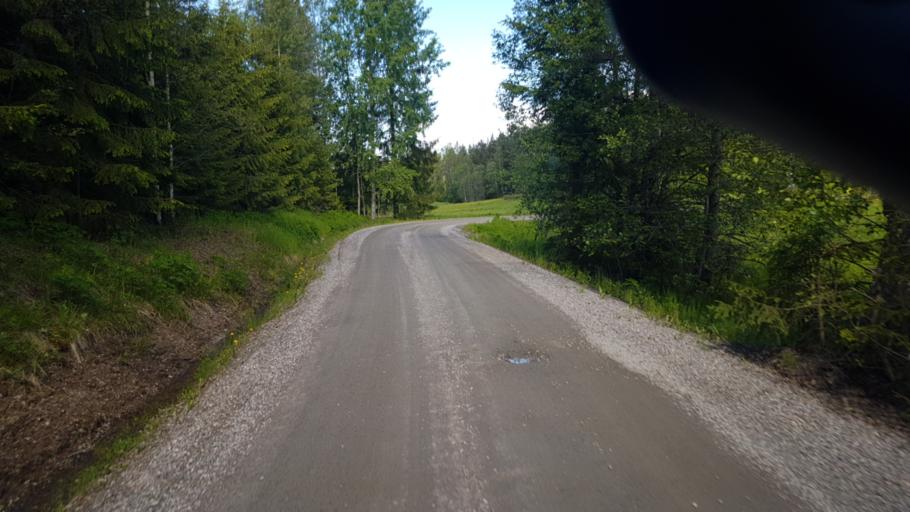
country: SE
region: Vaermland
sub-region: Grums Kommun
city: Slottsbron
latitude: 59.4629
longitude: 12.9191
